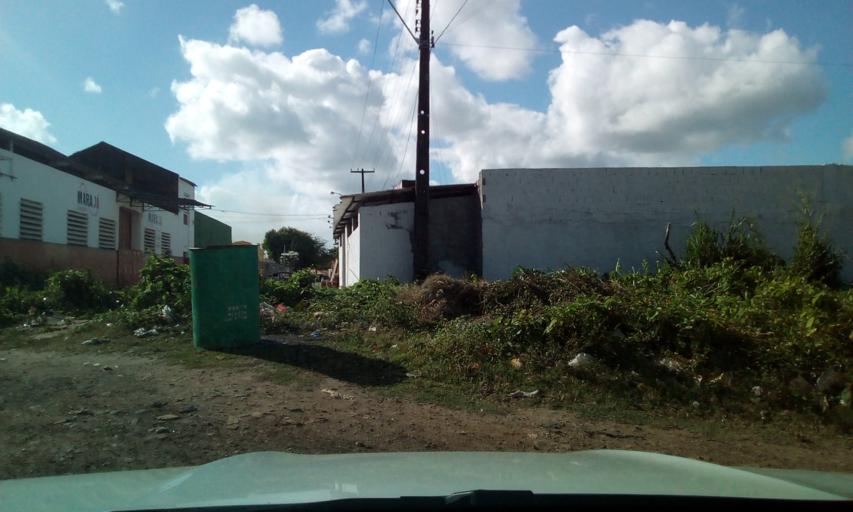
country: BR
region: Paraiba
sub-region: Joao Pessoa
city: Joao Pessoa
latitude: -7.1117
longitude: -34.8879
